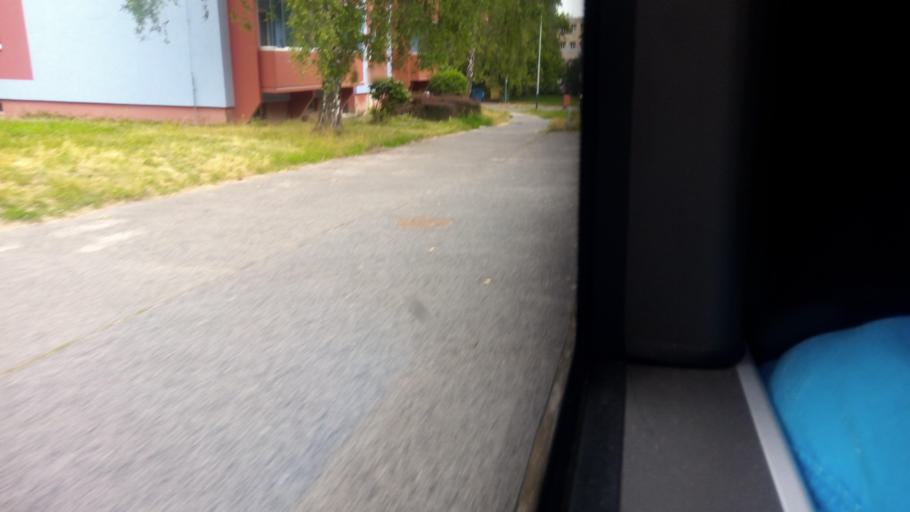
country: CZ
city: Vresina
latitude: 49.8372
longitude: 18.1839
